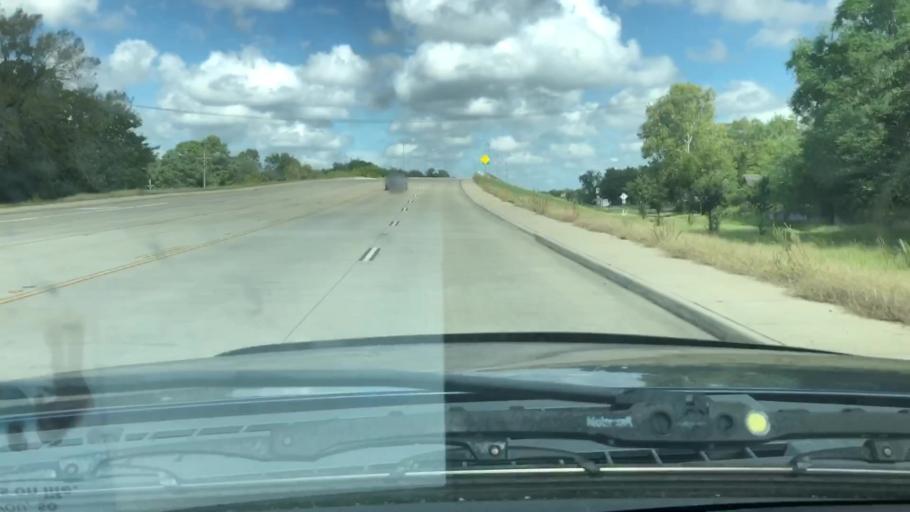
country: US
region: Texas
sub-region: Bowie County
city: Texarkana
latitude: 33.4113
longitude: -94.0606
